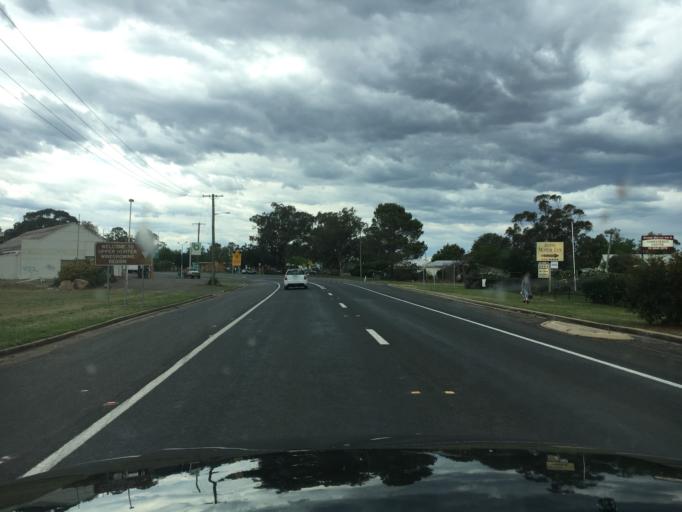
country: AU
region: New South Wales
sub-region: Muswellbrook
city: Muswellbrook
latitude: -32.0432
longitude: 150.8657
